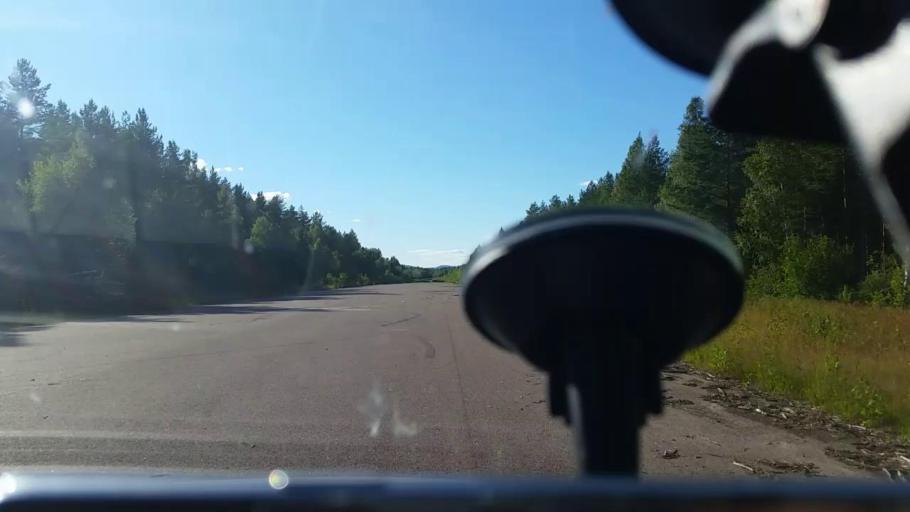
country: SE
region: Dalarna
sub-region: Borlange Kommun
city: Ornas
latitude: 60.4024
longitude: 15.5644
